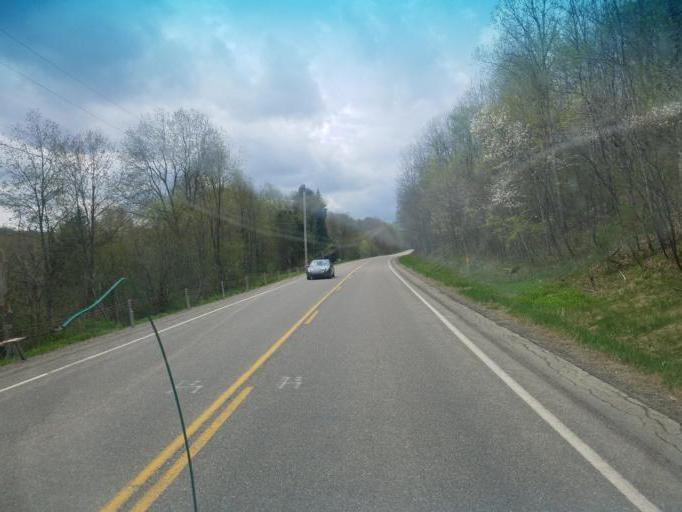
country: US
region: New York
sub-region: Allegany County
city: Wellsville
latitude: 42.0039
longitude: -77.8527
